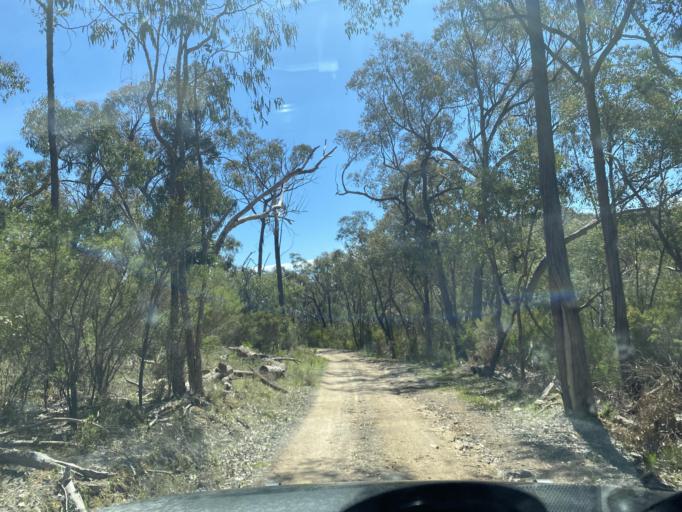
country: AU
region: Victoria
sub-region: Benalla
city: Benalla
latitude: -36.6991
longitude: 146.1522
